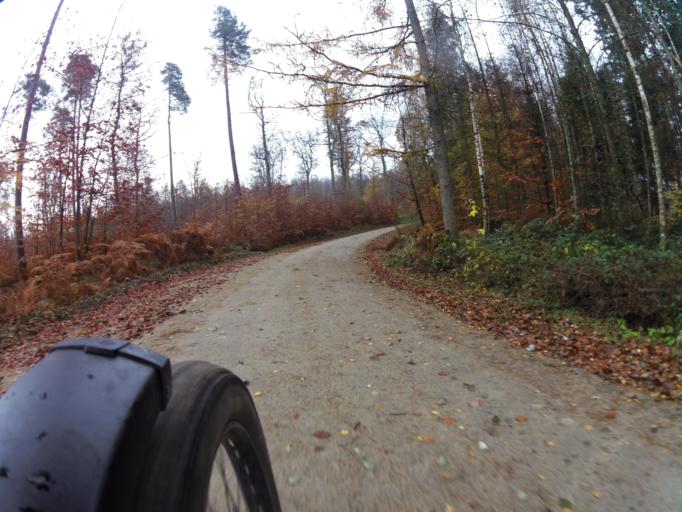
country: PL
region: Pomeranian Voivodeship
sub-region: Powiat pucki
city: Krokowa
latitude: 54.7683
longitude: 18.0953
